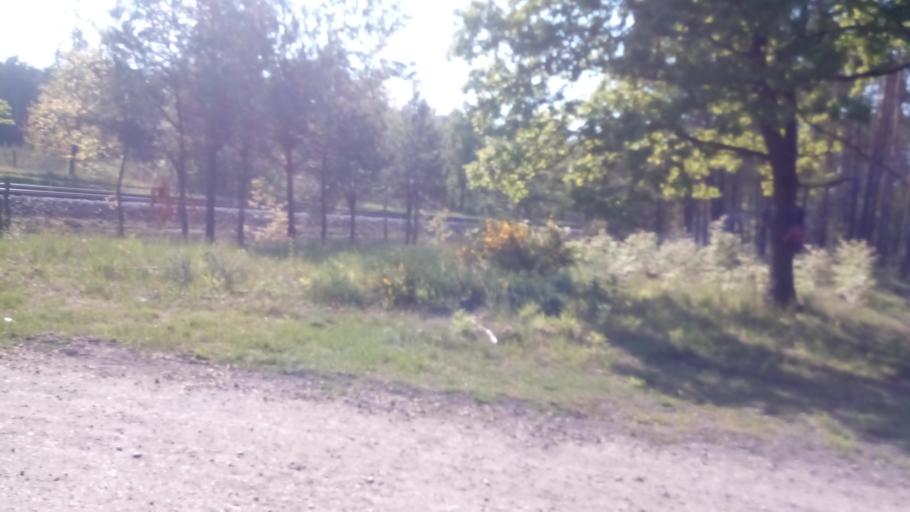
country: PL
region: Opole Voivodeship
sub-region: Powiat opolski
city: Tarnow Opolski
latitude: 50.5885
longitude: 18.0470
